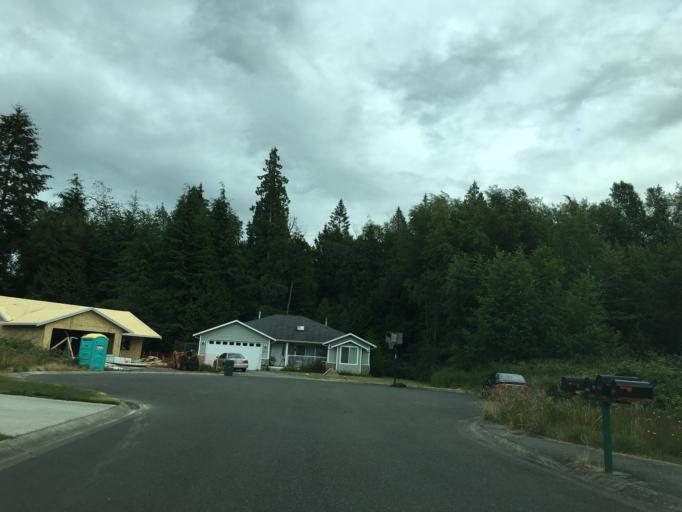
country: US
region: Washington
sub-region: Whatcom County
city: Birch Bay
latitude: 48.9464
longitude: -122.7381
